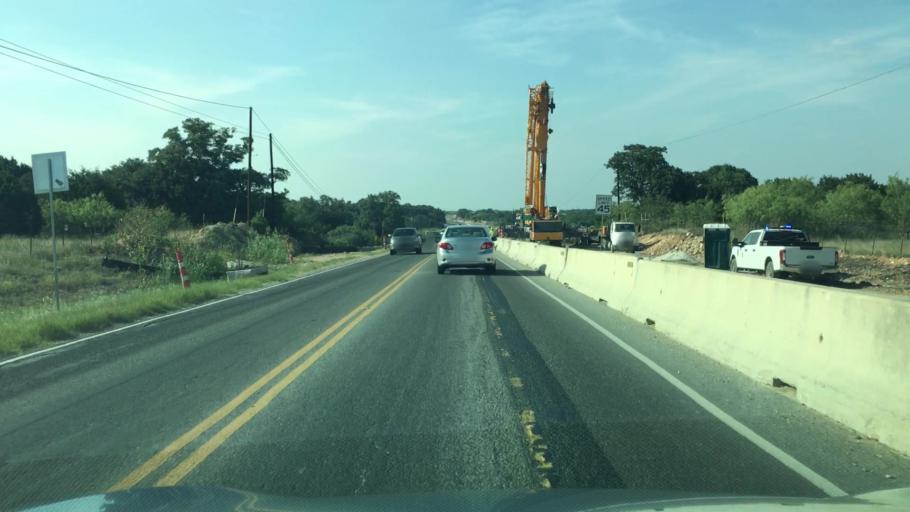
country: US
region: Texas
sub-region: Hays County
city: Buda
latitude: 30.0673
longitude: -97.8740
